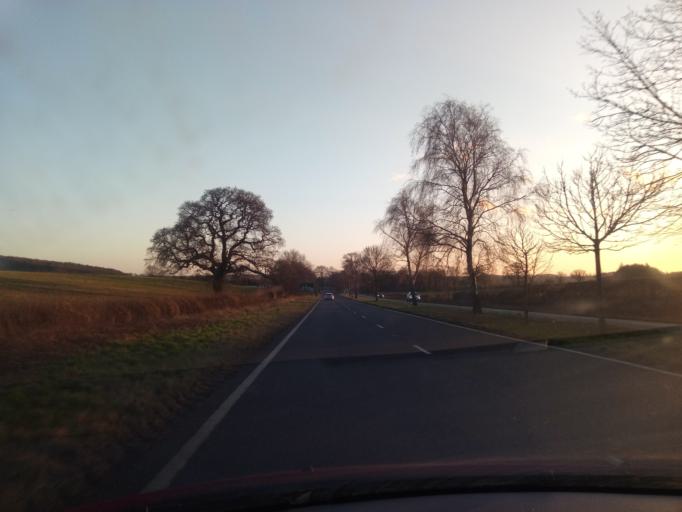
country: GB
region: England
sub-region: Nottinghamshire
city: Farnsfield
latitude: 53.0564
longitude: -1.0693
